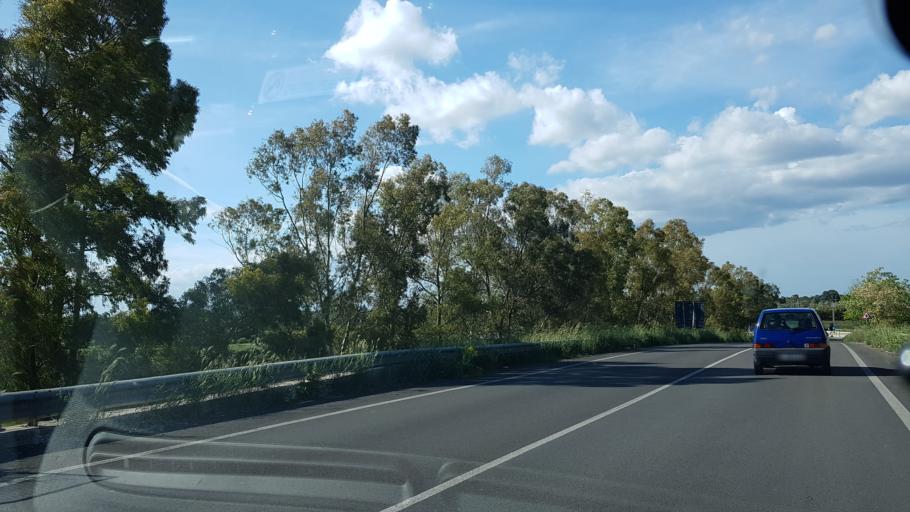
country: IT
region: Apulia
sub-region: Provincia di Brindisi
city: Mesagne
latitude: 40.5601
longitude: 17.7879
